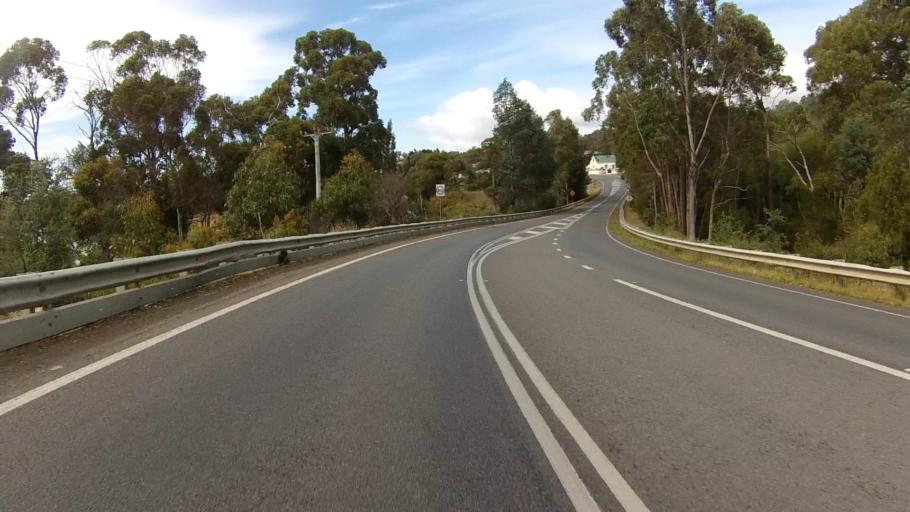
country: AU
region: Tasmania
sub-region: Kingborough
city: Kettering
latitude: -43.1210
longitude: 147.2462
